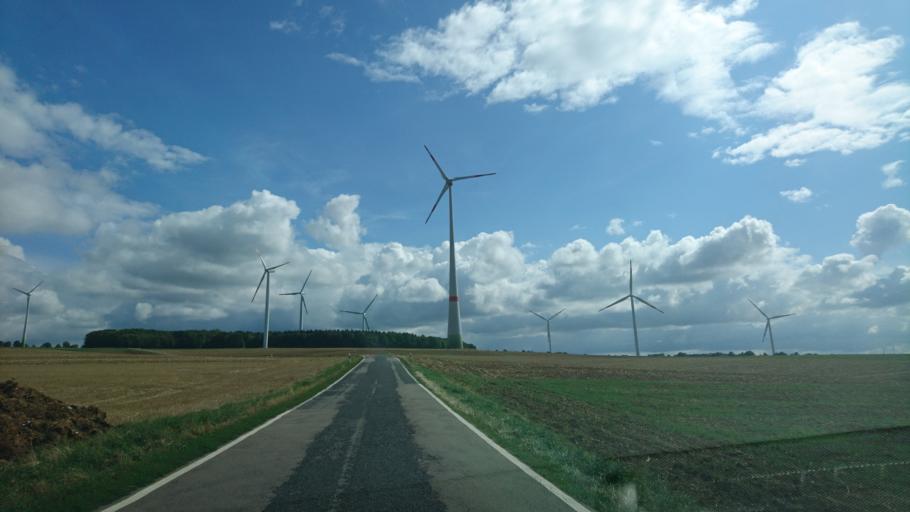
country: DE
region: Rheinland-Pfalz
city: Merzkirchen
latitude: 49.5673
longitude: 6.4658
